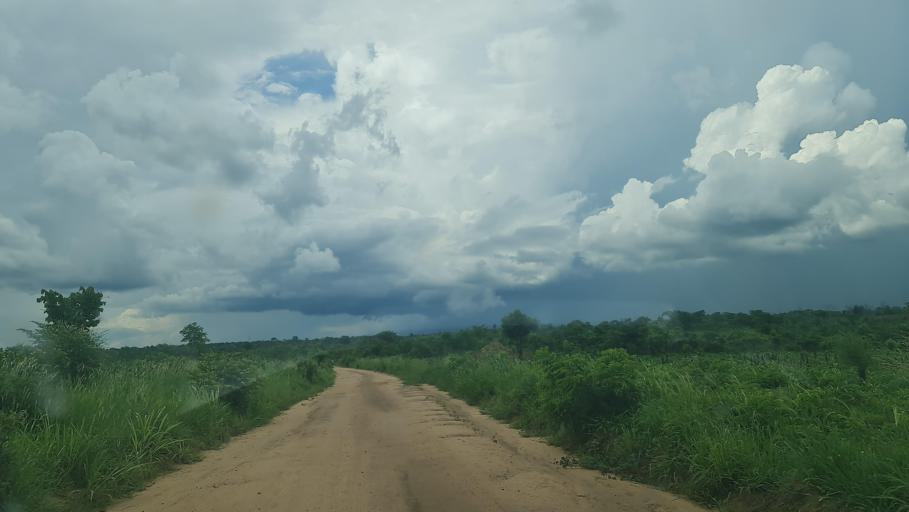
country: MW
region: Southern Region
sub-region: Nsanje District
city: Nsanje
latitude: -17.5740
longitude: 35.6550
